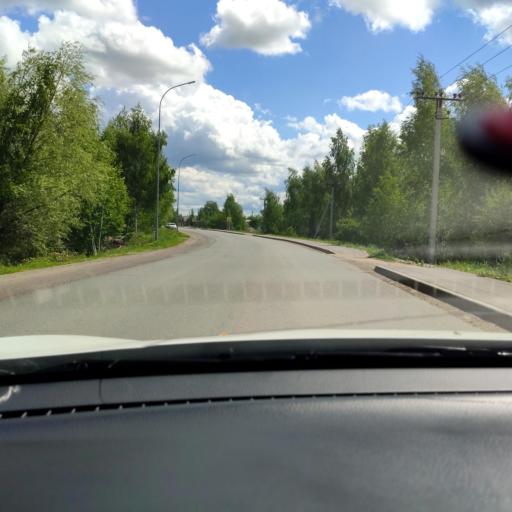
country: RU
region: Tatarstan
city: Stolbishchi
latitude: 55.6947
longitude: 49.1999
